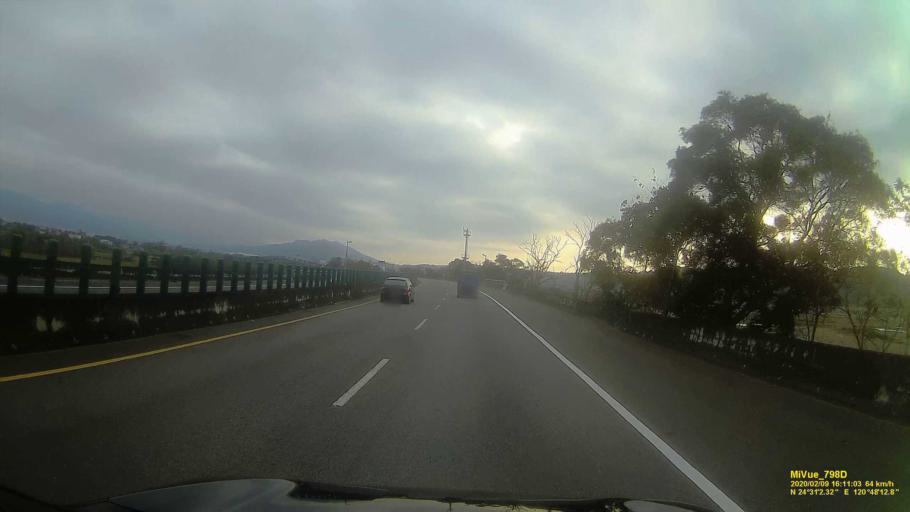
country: TW
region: Taiwan
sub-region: Miaoli
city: Miaoli
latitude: 24.5169
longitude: 120.8033
